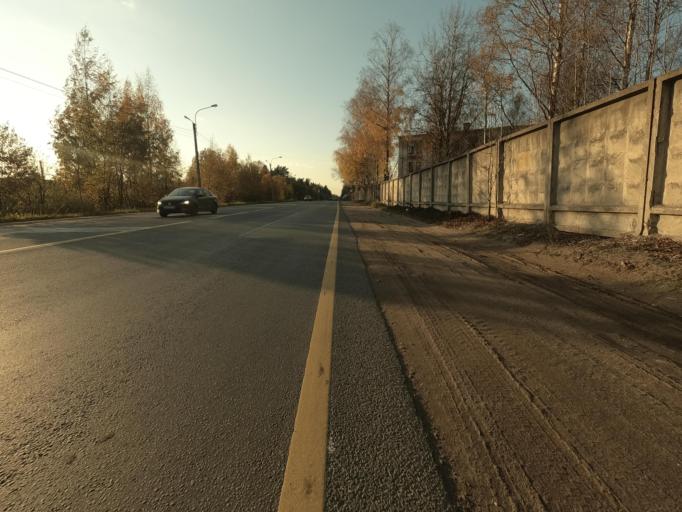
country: RU
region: St.-Petersburg
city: Pesochnyy
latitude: 60.1773
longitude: 30.1521
